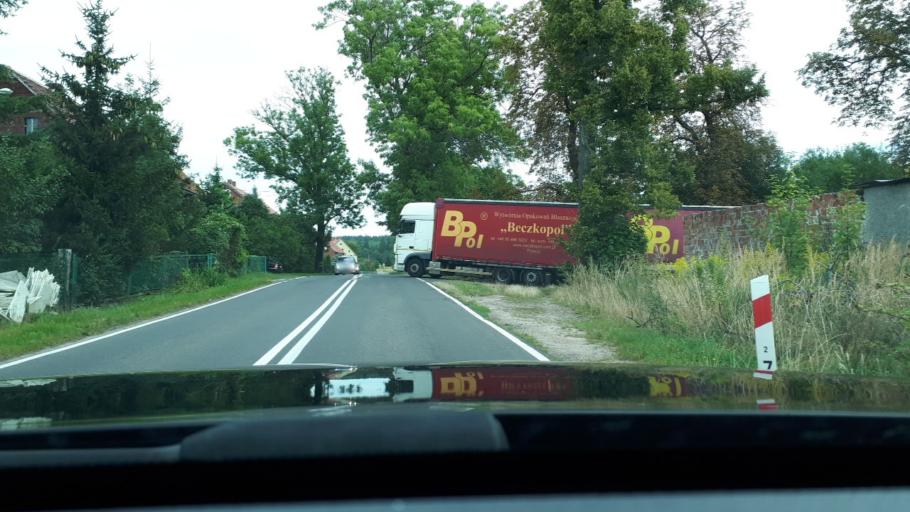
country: PL
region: Lower Silesian Voivodeship
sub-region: Powiat lwowecki
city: Gryfow Slaski
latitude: 51.0462
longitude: 15.4481
